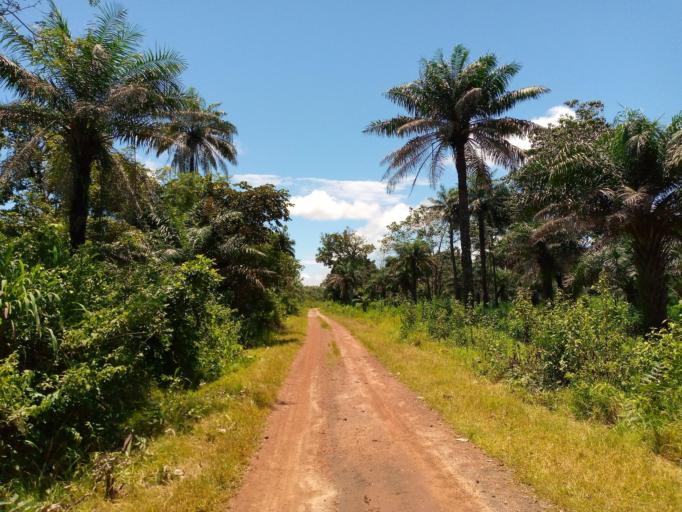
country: SL
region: Northern Province
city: Binkolo
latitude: 9.0933
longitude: -12.1420
